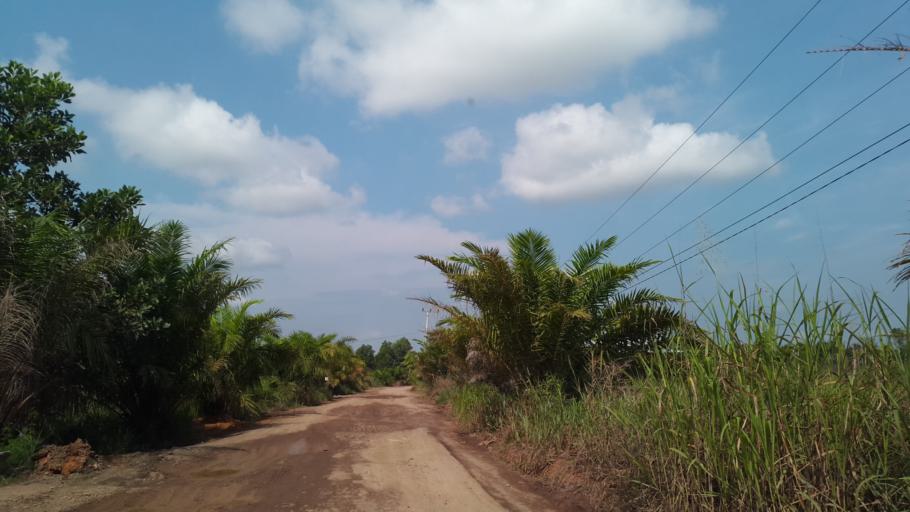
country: ID
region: South Sumatra
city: Plaju
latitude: -3.1431
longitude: 104.6878
